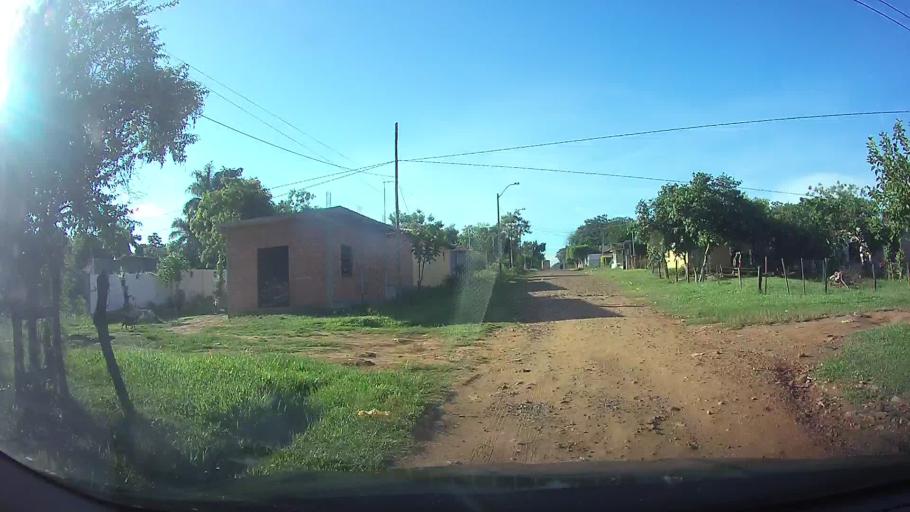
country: PY
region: Central
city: Limpio
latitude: -25.2541
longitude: -57.4683
